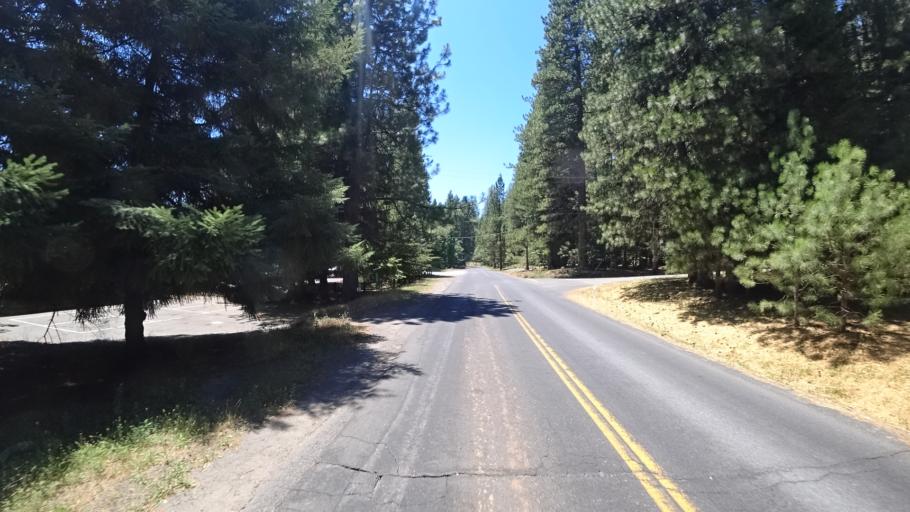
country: US
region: California
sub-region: Calaveras County
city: Arnold
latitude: 38.2509
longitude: -120.3333
